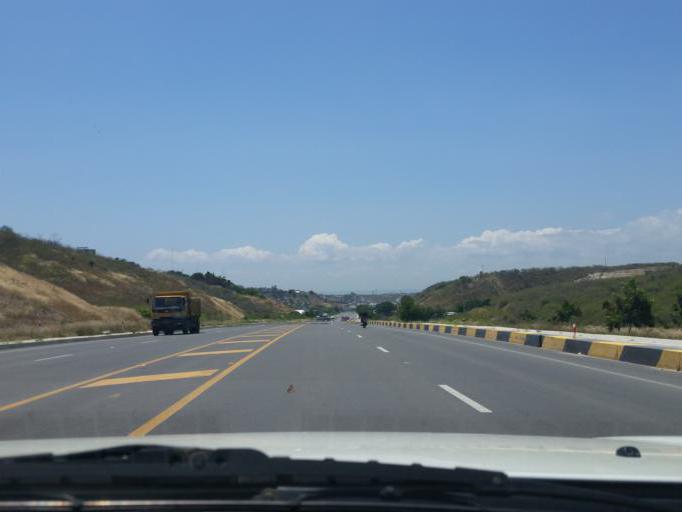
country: EC
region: Manabi
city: Manta
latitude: -0.9610
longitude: -80.7511
